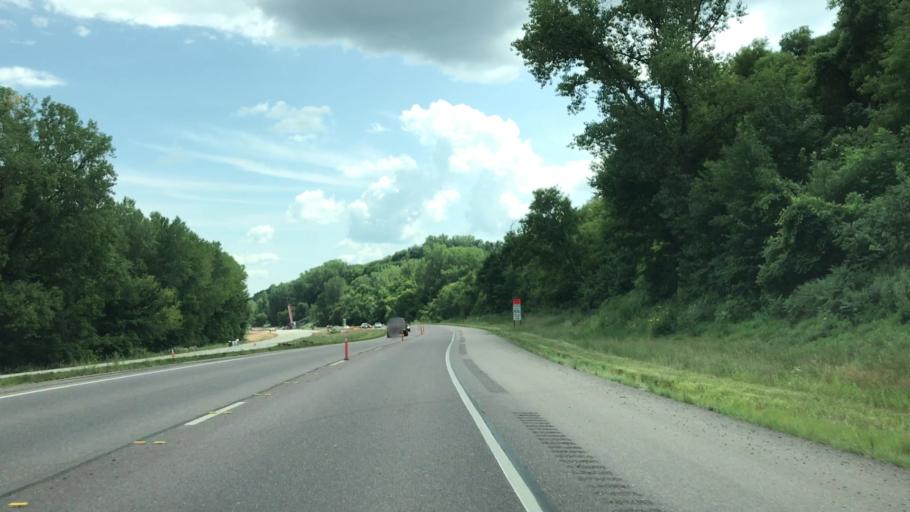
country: US
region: Minnesota
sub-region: Nicollet County
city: Saint Peter
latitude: 44.3690
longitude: -93.9654
